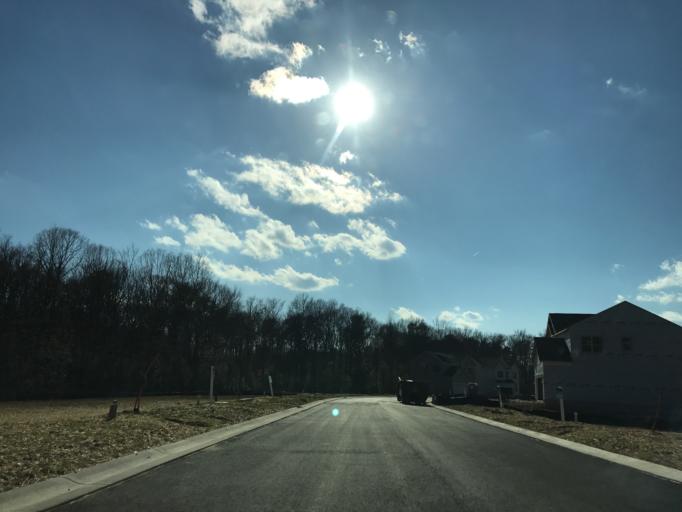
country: US
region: Maryland
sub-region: Anne Arundel County
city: Green Haven
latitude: 39.1532
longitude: -76.5753
